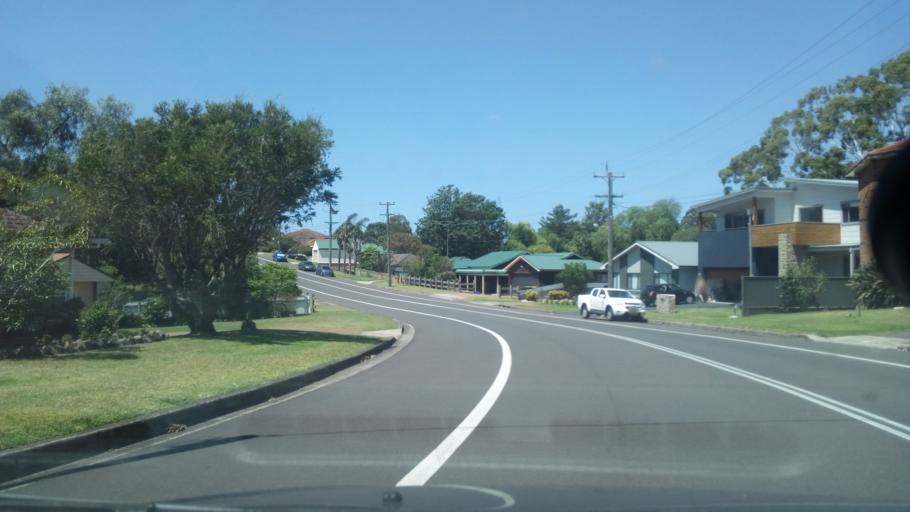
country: AU
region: New South Wales
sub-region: Wollongong
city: West Wollongong
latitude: -34.4270
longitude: 150.8572
